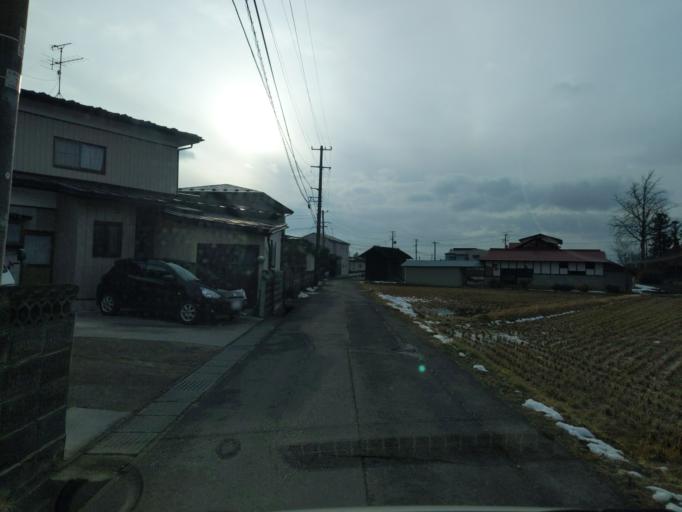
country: JP
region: Iwate
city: Mizusawa
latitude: 39.1729
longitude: 141.1377
